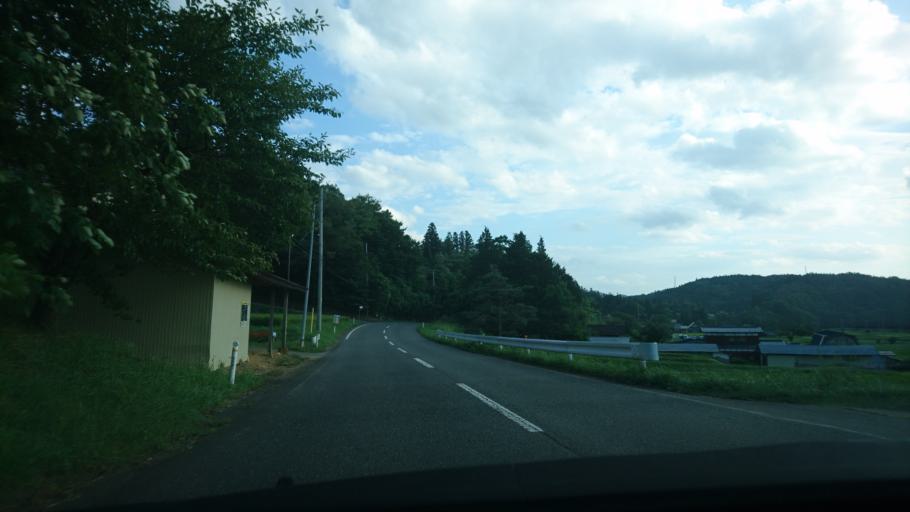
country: JP
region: Iwate
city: Ichinoseki
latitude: 39.0232
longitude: 141.2914
